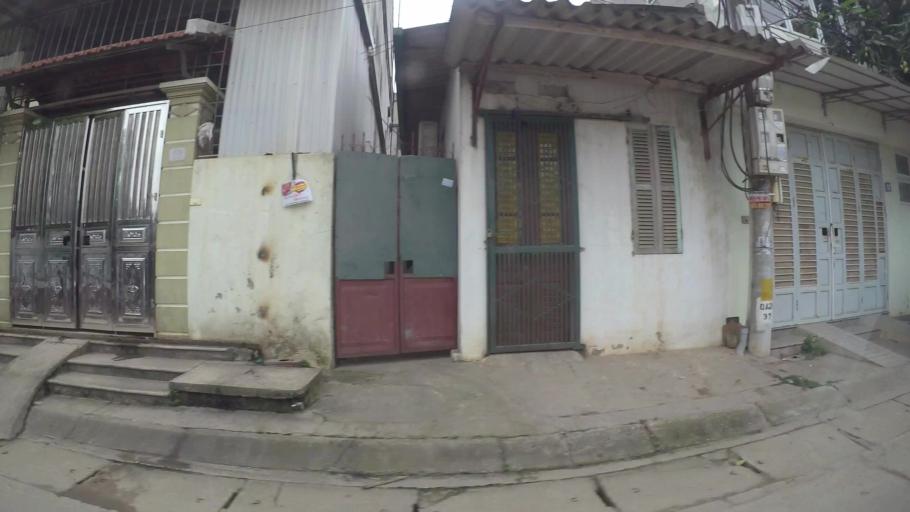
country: VN
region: Ha Noi
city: Tay Ho
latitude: 21.0652
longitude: 105.8365
